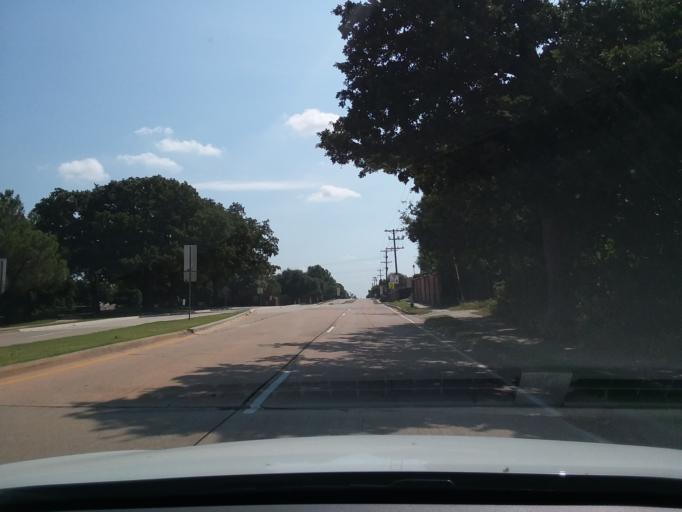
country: US
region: Texas
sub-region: Denton County
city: Lewisville
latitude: 33.0208
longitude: -97.0421
